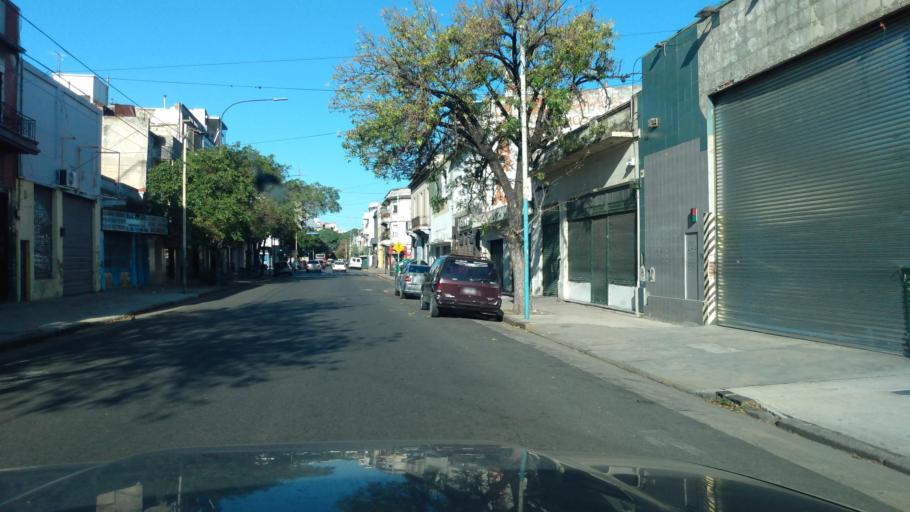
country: AR
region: Buenos Aires F.D.
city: Colegiales
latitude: -34.6006
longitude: -58.4472
